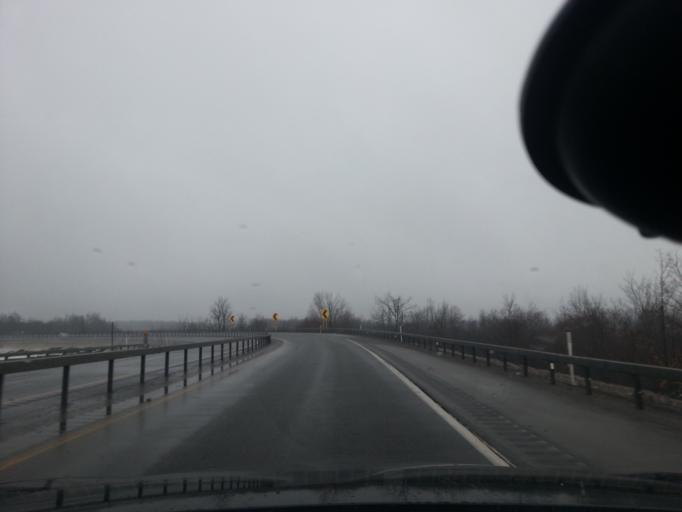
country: US
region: New York
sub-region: Jefferson County
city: Watertown
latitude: 44.0448
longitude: -75.9159
